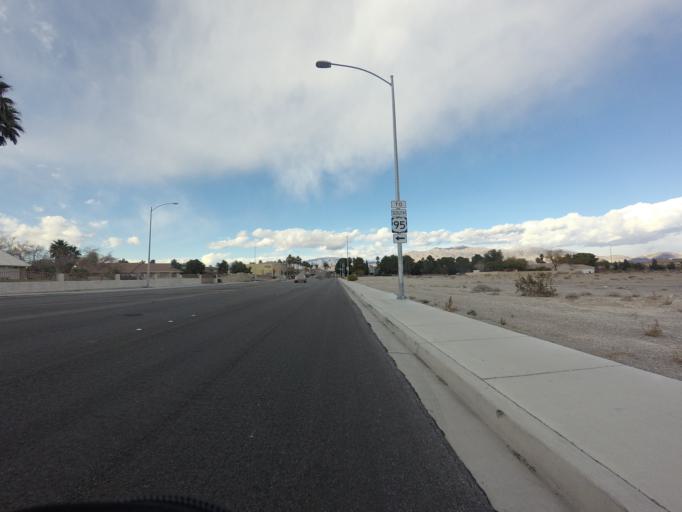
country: US
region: Nevada
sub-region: Clark County
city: Las Vegas
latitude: 36.2717
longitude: -115.2515
